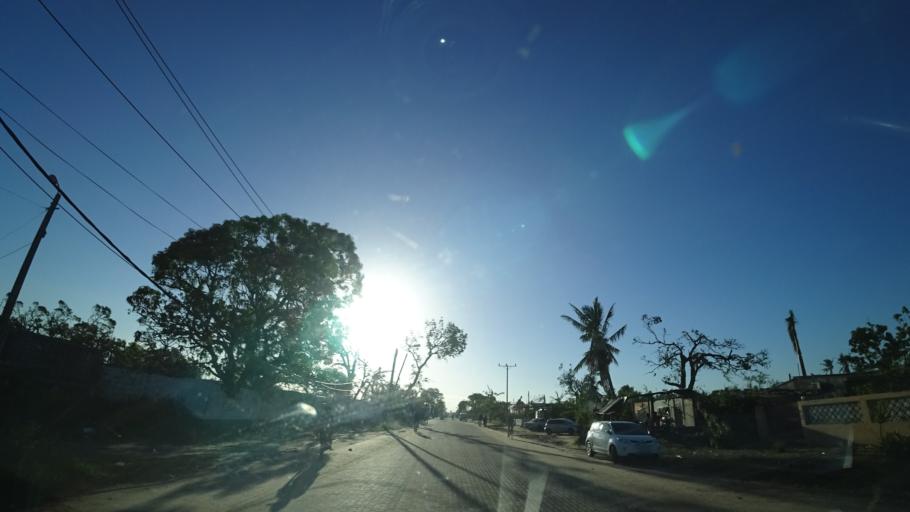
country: MZ
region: Sofala
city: Beira
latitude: -19.7472
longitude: 34.8493
